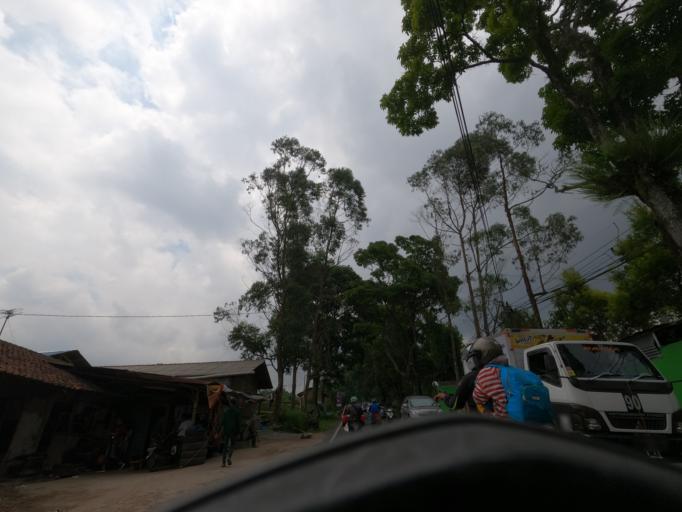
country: ID
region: West Java
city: Sukabumi
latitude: -6.7689
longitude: 107.0587
